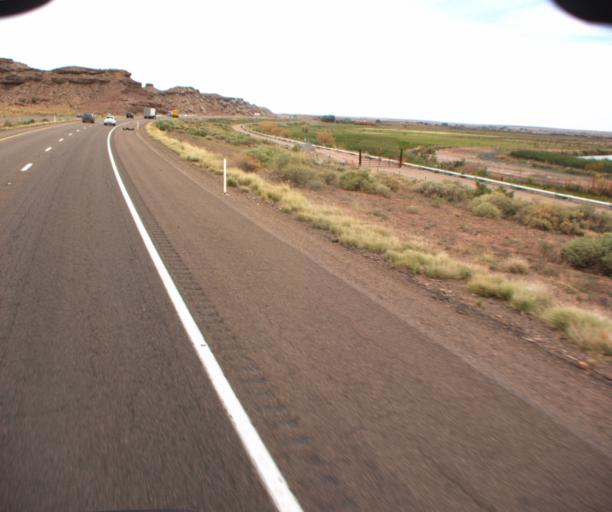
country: US
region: Arizona
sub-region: Navajo County
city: Joseph City
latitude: 34.9406
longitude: -110.2824
